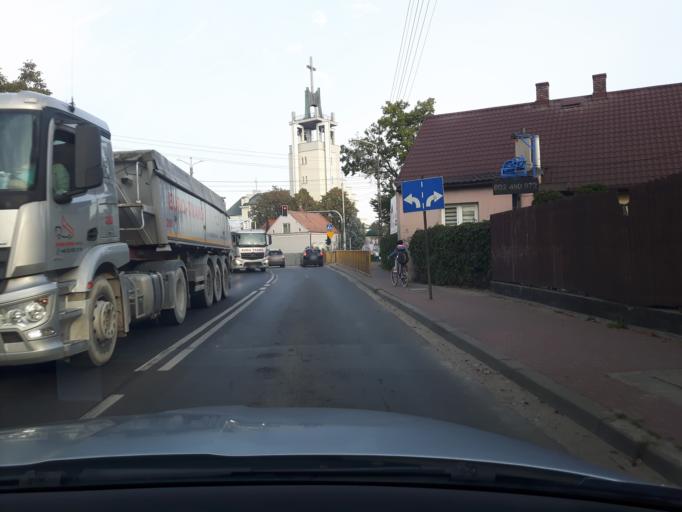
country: PL
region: Masovian Voivodeship
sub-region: Powiat wolominski
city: Zabki
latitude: 52.2865
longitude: 21.1085
